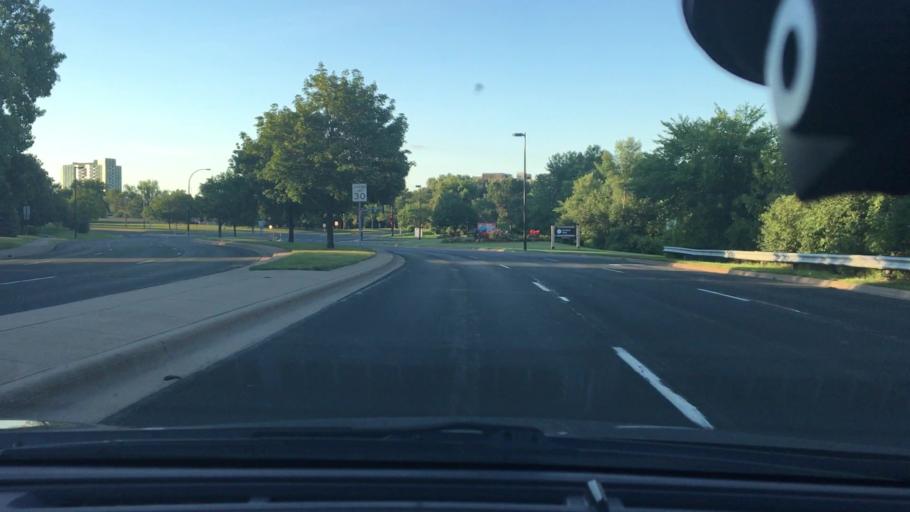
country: US
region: Minnesota
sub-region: Hennepin County
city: Edina
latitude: 44.8849
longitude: -93.3329
